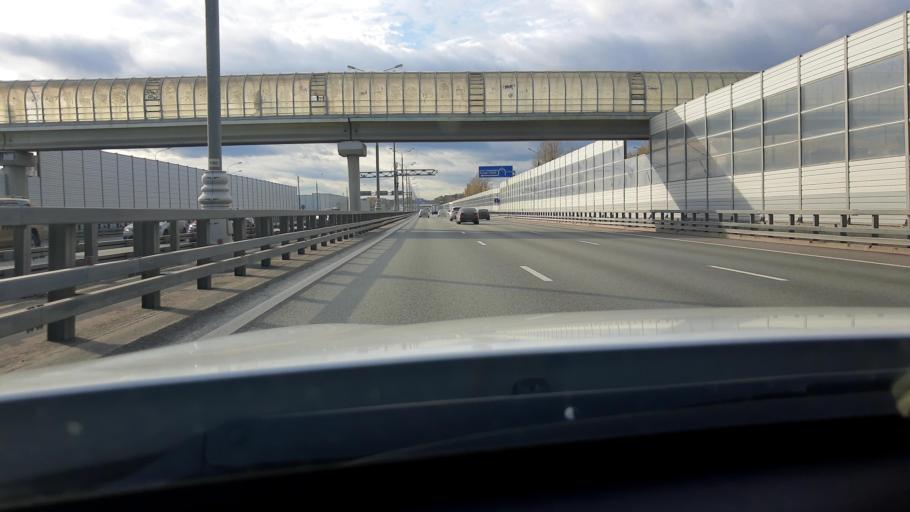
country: RU
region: Moskovskaya
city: Aprelevka
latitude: 55.5370
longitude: 37.0700
